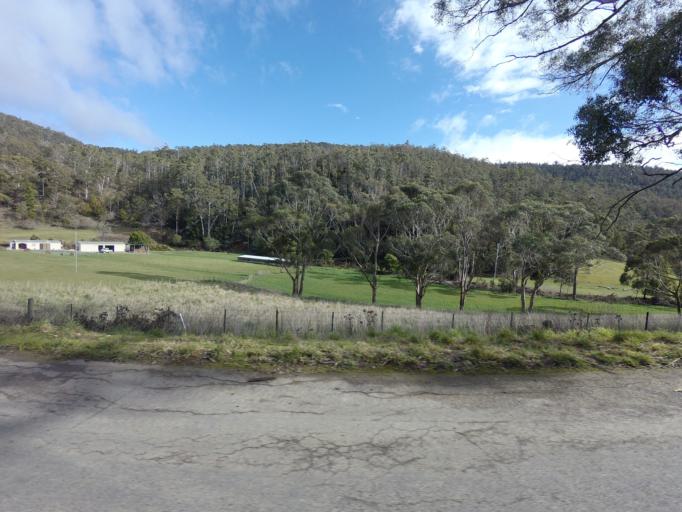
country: AU
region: Tasmania
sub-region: Derwent Valley
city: New Norfolk
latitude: -42.7894
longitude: 146.9462
